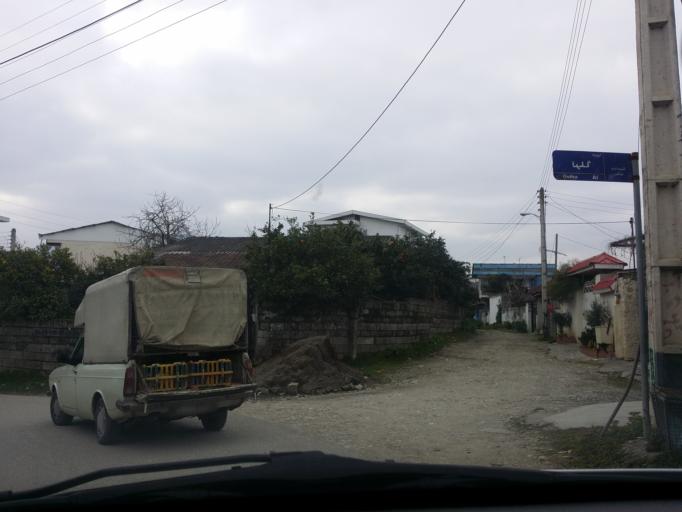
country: IR
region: Mazandaran
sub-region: Nowshahr
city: Nowshahr
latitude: 36.6488
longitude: 51.4774
